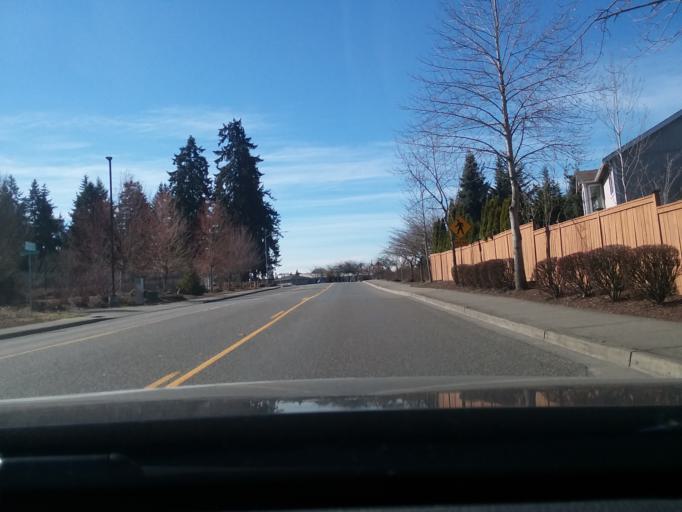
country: US
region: Washington
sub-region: Pierce County
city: Puyallup
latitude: 47.1641
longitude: -122.2862
